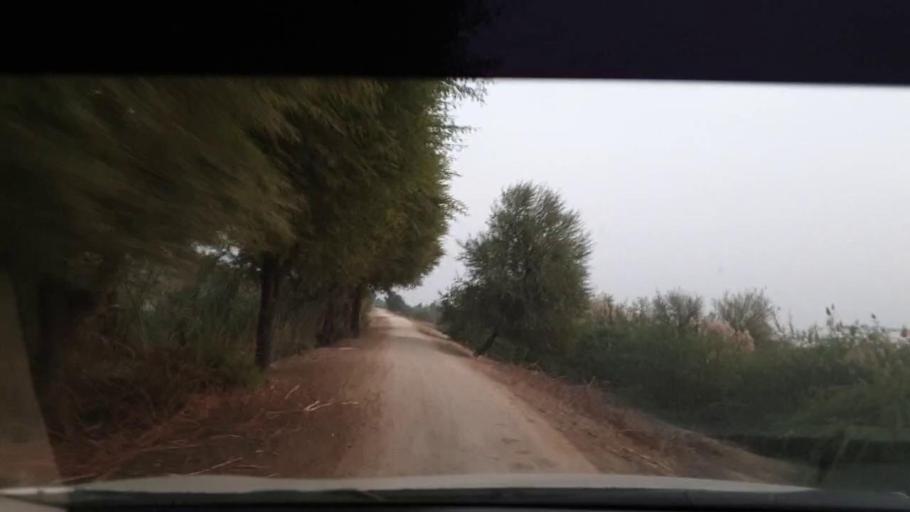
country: PK
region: Sindh
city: Berani
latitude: 25.8474
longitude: 68.7857
